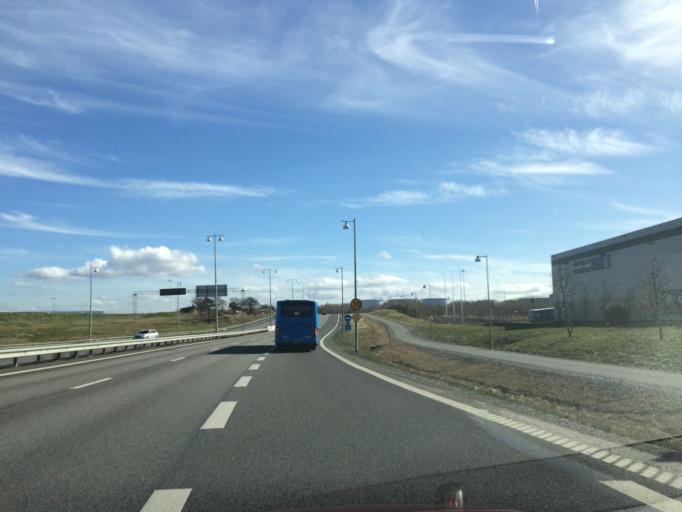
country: SE
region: Vaestra Goetaland
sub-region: Goteborg
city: Torslanda
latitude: 57.7174
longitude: 11.8211
